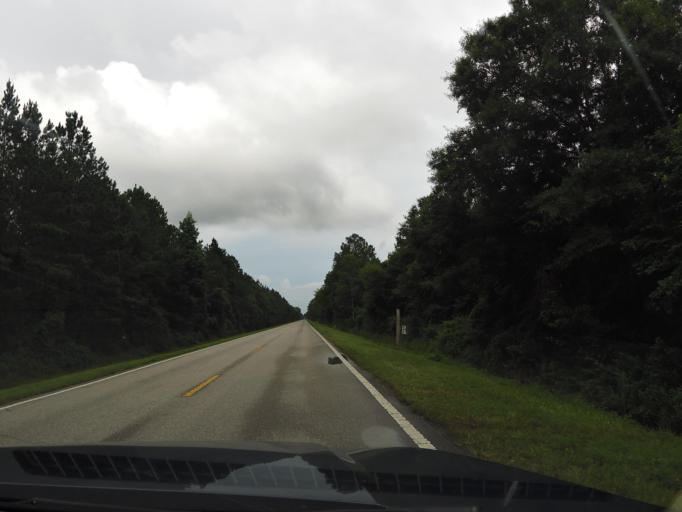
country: US
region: Florida
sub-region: Saint Johns County
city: Saint Augustine South
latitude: 29.8561
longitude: -81.4521
